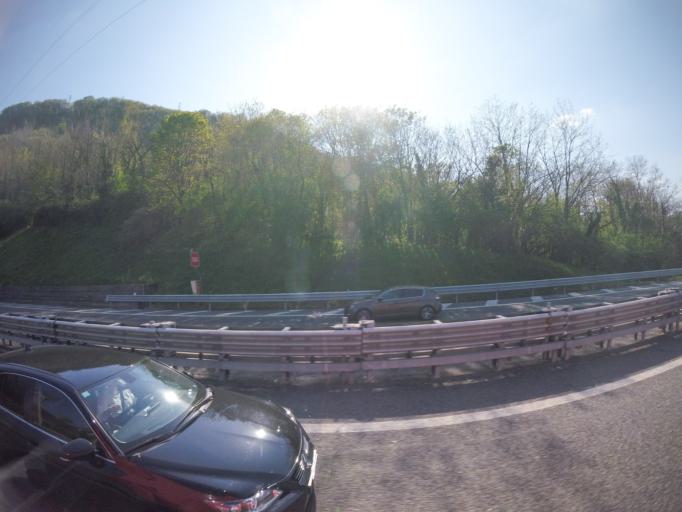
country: CH
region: Ticino
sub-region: Mendrisio District
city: Chiasso
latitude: 45.8262
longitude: 9.0449
